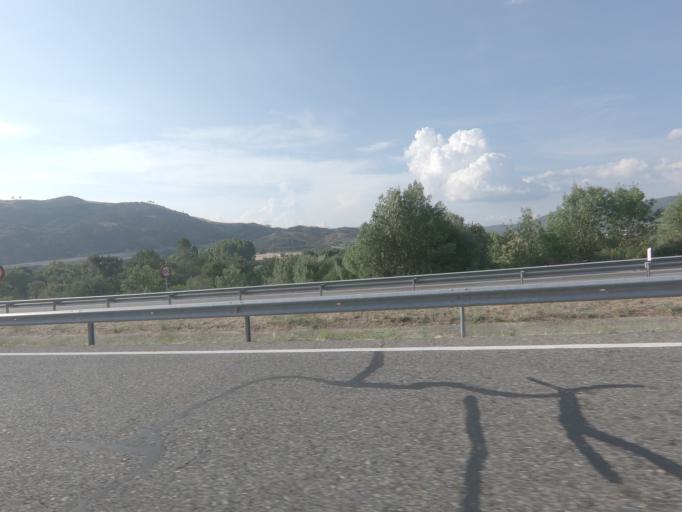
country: ES
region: Galicia
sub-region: Provincia de Ourense
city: Oimbra
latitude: 41.9253
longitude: -7.4945
